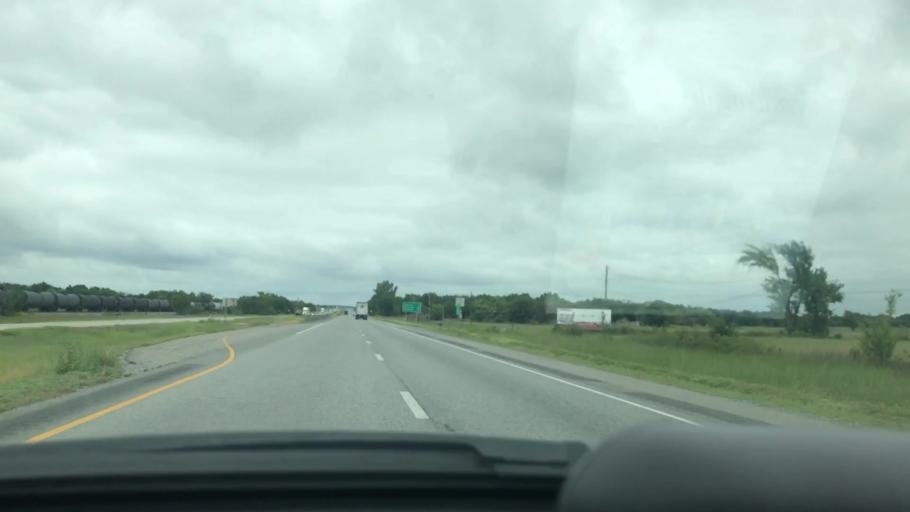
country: US
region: Oklahoma
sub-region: Pittsburg County
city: McAlester
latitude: 34.7378
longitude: -95.8990
